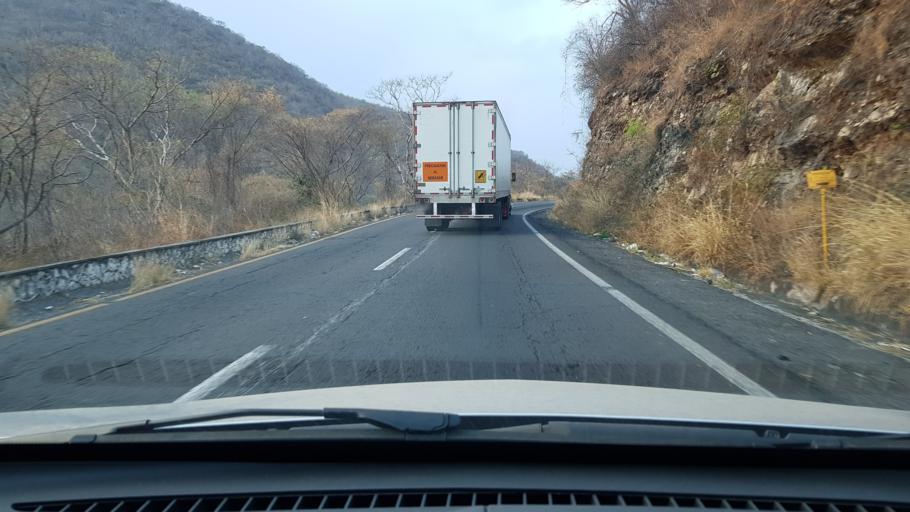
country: MX
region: Morelos
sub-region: Jiutepec
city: Independencia
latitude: 18.8623
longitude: -99.1218
